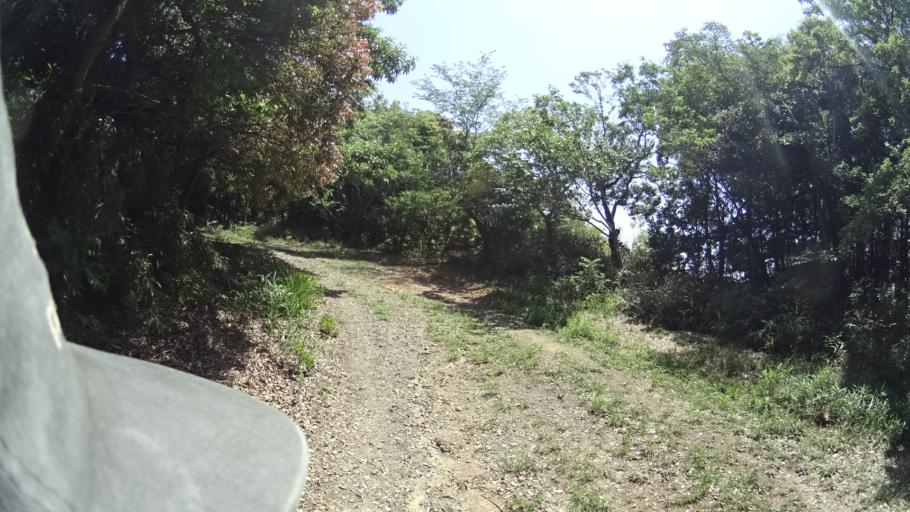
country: JP
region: Shizuoka
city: Kosai-shi
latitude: 34.7378
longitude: 137.4862
